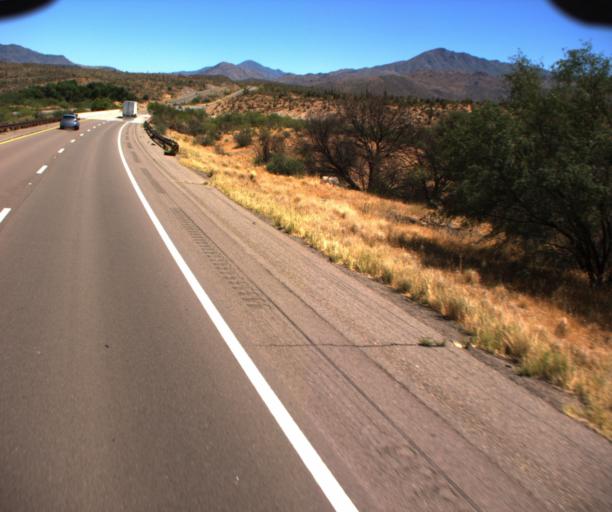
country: US
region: Arizona
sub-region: Maricopa County
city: Rio Verde
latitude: 33.7266
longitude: -111.5111
